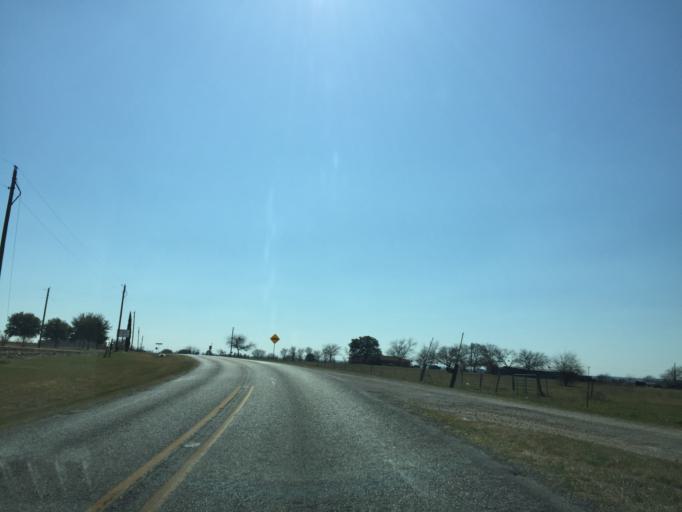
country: US
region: Texas
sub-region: Williamson County
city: Georgetown
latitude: 30.6835
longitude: -97.5895
